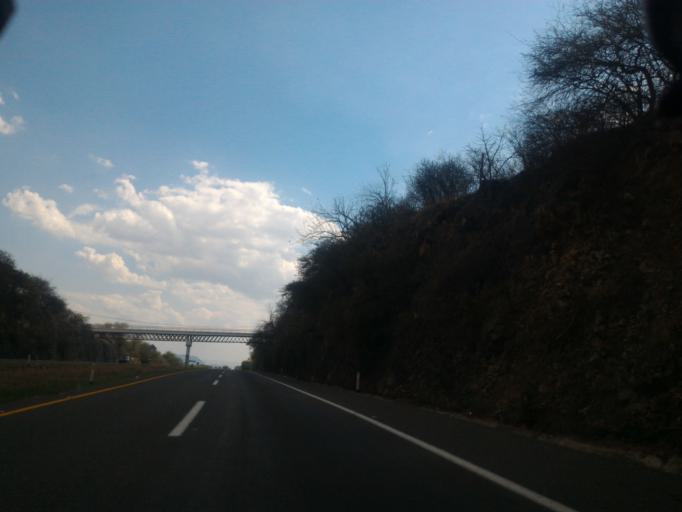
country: MX
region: Jalisco
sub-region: Acatlan de Juarez
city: Villa de los Ninos
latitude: 20.3520
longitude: -103.5759
